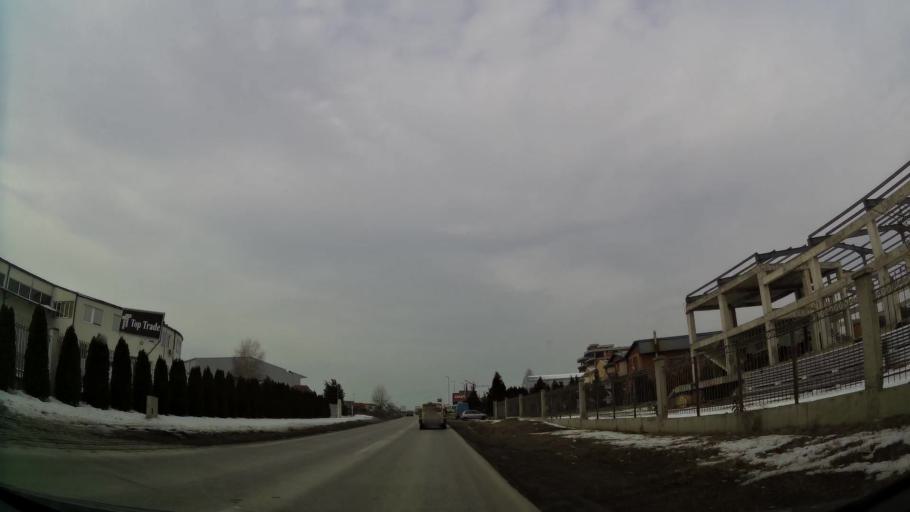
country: MK
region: Suto Orizari
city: Suto Orizare
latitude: 42.0424
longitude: 21.3921
